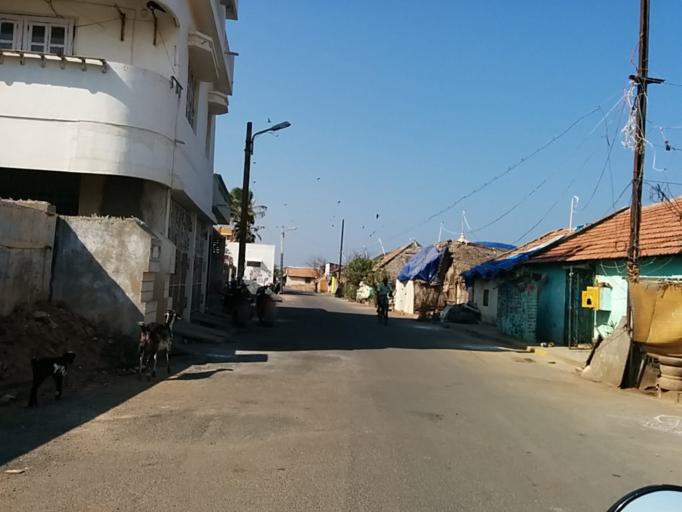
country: IN
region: Pondicherry
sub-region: Puducherry
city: Puducherry
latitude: 11.9410
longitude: 79.8370
